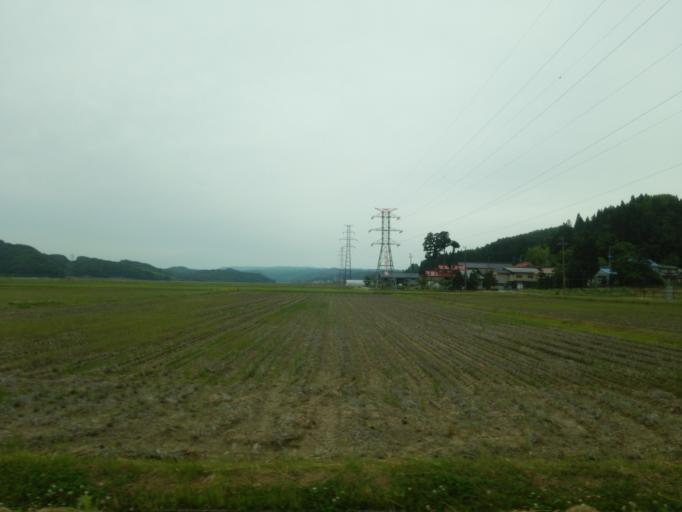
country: JP
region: Fukushima
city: Inawashiro
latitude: 37.4913
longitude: 140.0098
